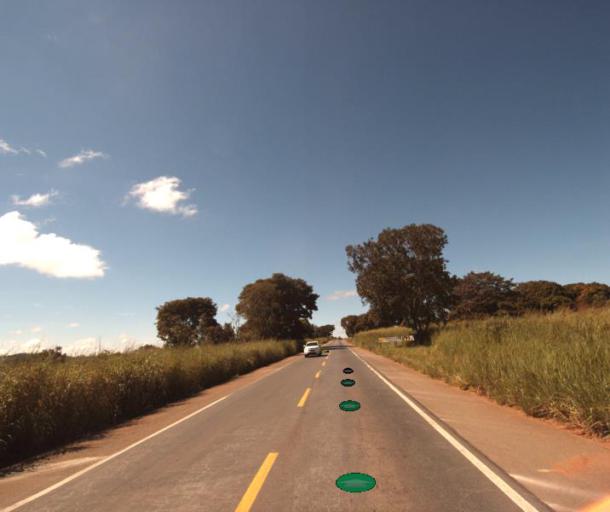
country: BR
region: Goias
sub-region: Jaragua
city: Jaragua
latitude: -15.5579
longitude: -49.4252
